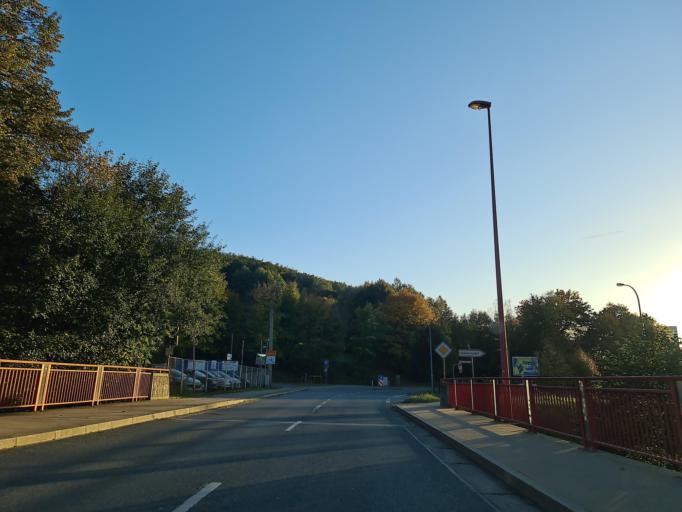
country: DE
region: Thuringia
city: Greiz
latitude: 50.6341
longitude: 12.1923
